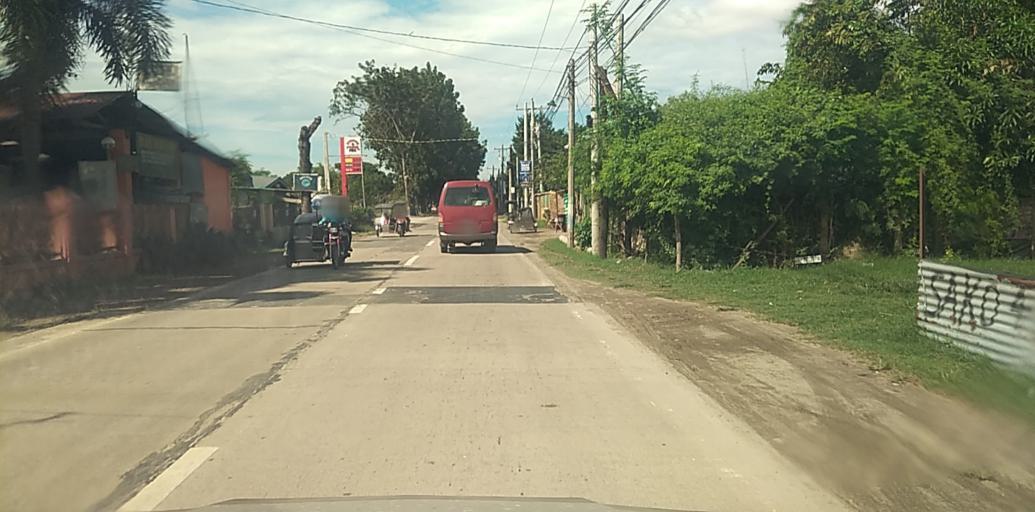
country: PH
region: Central Luzon
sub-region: Province of Pampanga
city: Arayat
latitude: 15.1506
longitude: 120.7464
